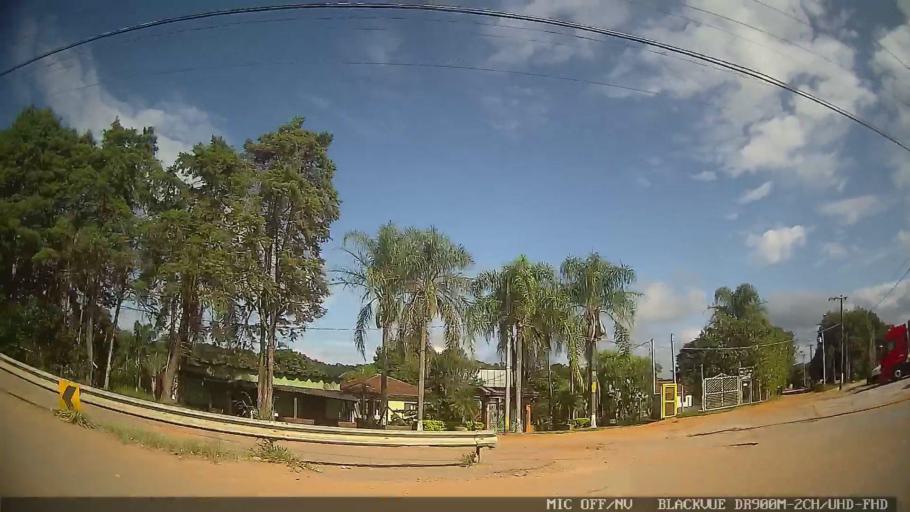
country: BR
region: Sao Paulo
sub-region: Jarinu
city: Jarinu
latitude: -23.0536
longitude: -46.6784
